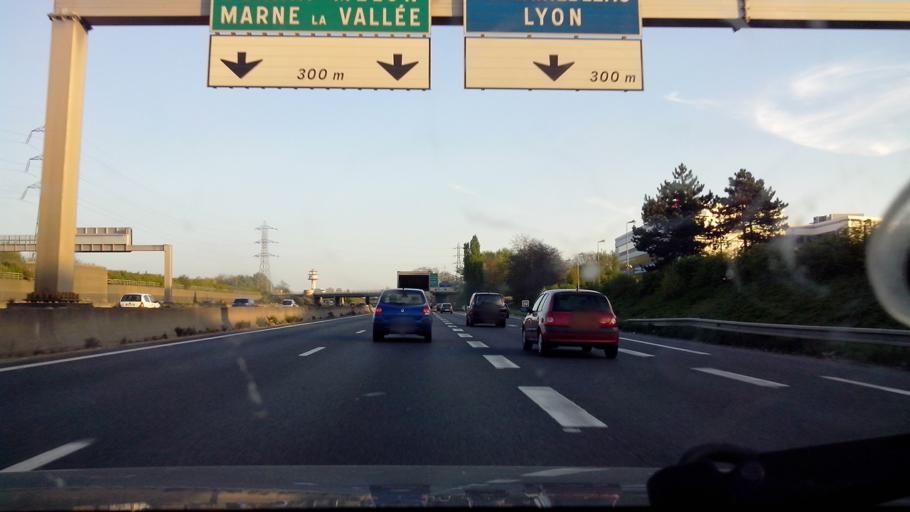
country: FR
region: Ile-de-France
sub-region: Departement de l'Essonne
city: Lisses
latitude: 48.6143
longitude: 2.4299
